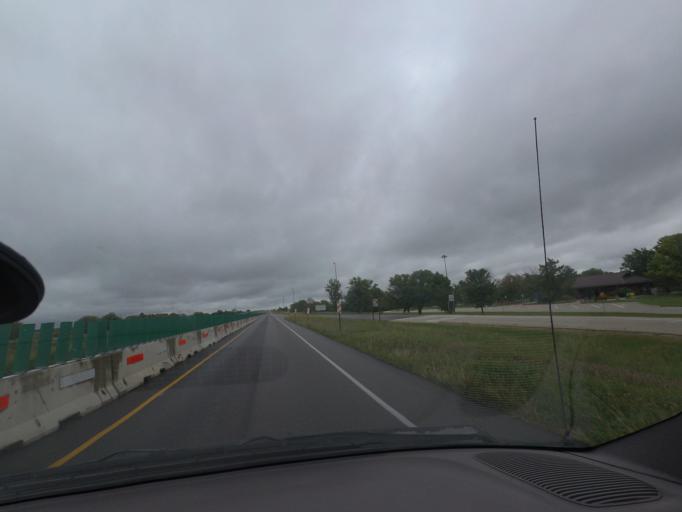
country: US
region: Illinois
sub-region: Piatt County
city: Cerro Gordo
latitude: 39.9920
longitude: -88.7840
